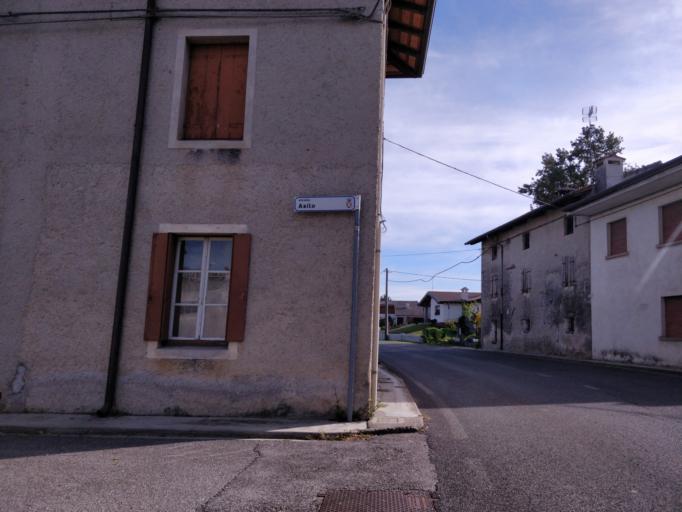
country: IT
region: Friuli Venezia Giulia
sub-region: Provincia di Udine
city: Bertiolo
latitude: 45.9434
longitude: 13.0246
